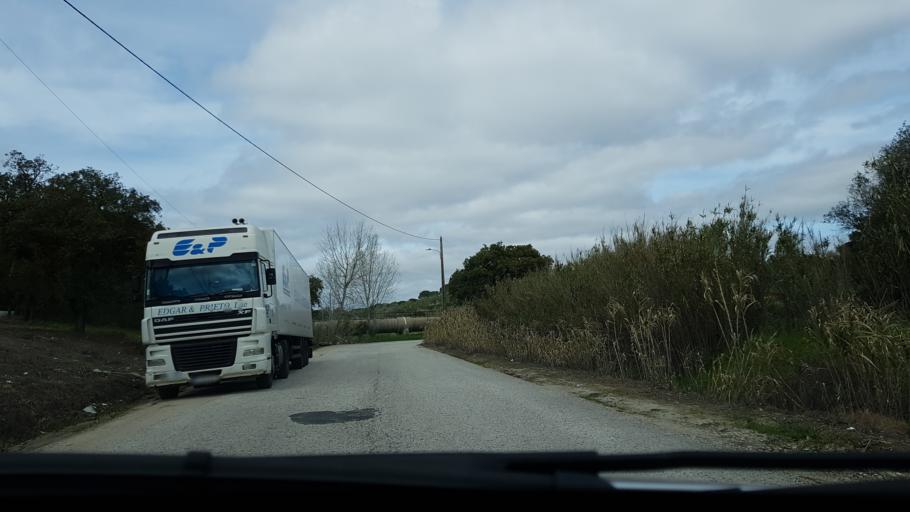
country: PT
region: Lisbon
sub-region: Alenquer
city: Carregado
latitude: 39.0429
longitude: -8.9312
